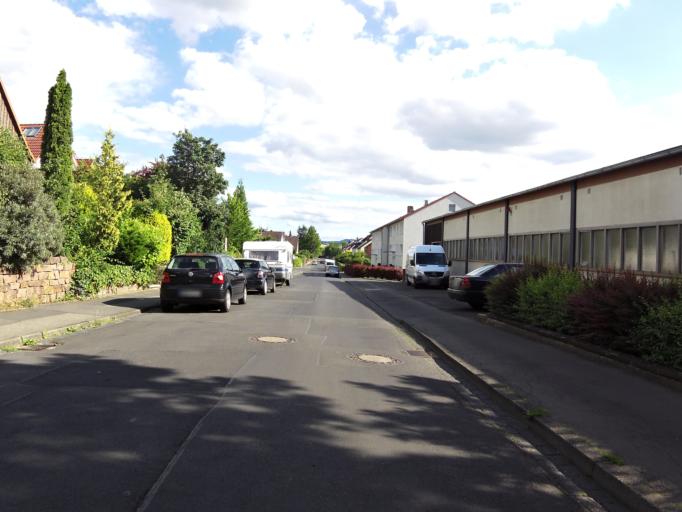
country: DE
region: Lower Saxony
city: Goettingen
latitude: 51.5119
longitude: 9.9585
